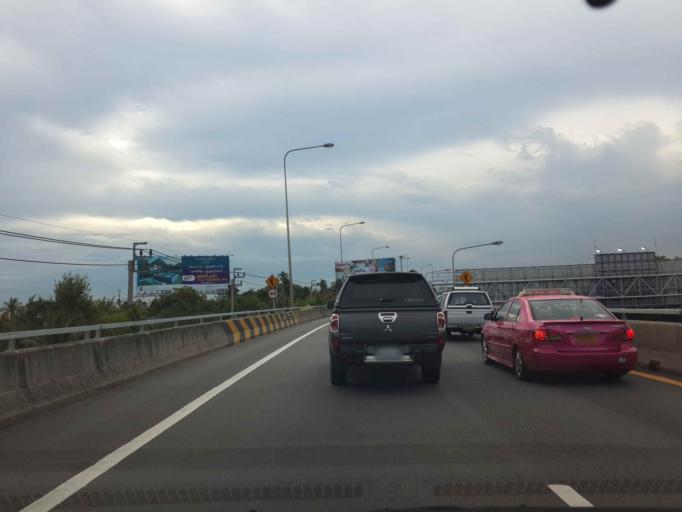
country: TH
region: Bangkok
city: Chom Thong
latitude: 13.6756
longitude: 100.4807
